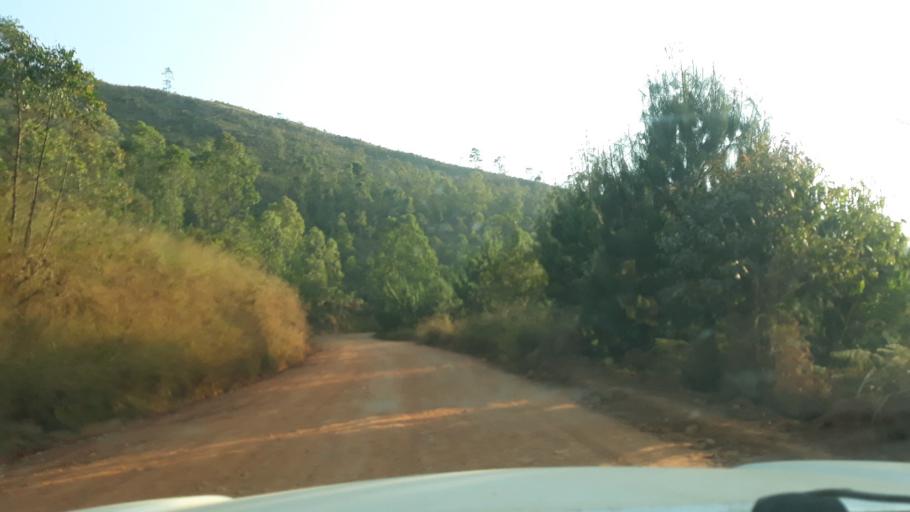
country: RW
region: Western Province
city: Cyangugu
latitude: -2.6984
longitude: 28.9047
